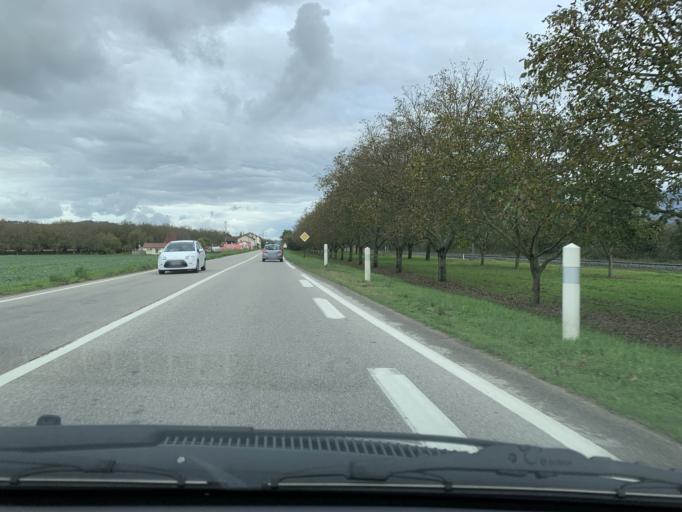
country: FR
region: Rhone-Alpes
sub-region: Departement de l'Isere
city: Chatte
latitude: 45.1261
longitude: 5.2827
